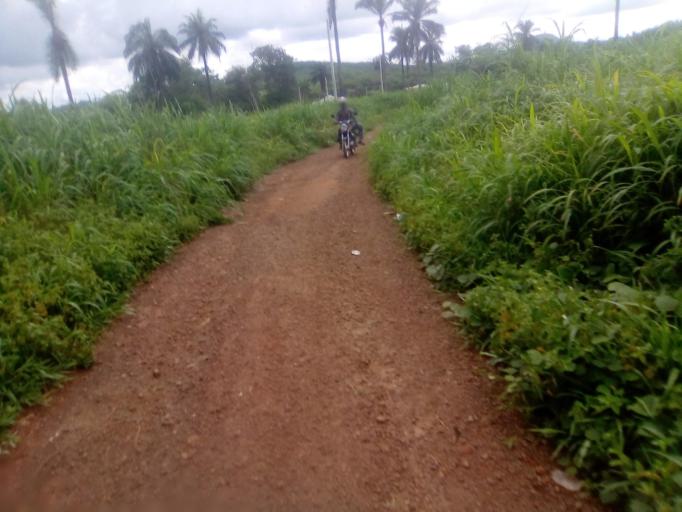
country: SL
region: Southern Province
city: Moyamba
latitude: 8.1458
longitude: -12.4380
